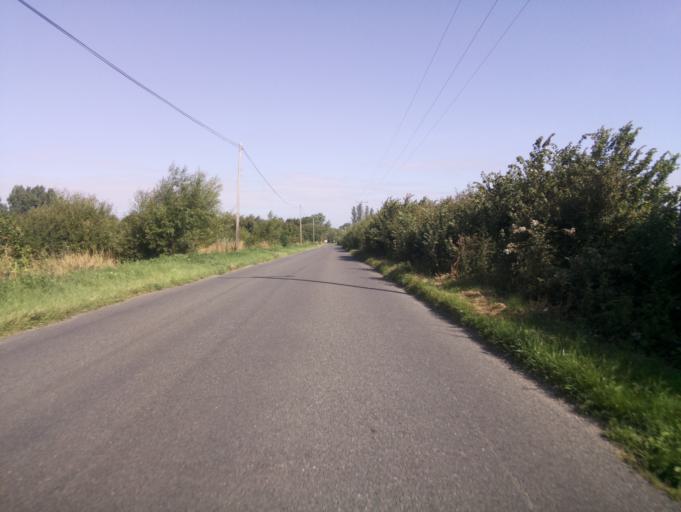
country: GB
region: England
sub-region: Oxfordshire
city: Bampton
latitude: 51.7177
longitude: -1.5300
